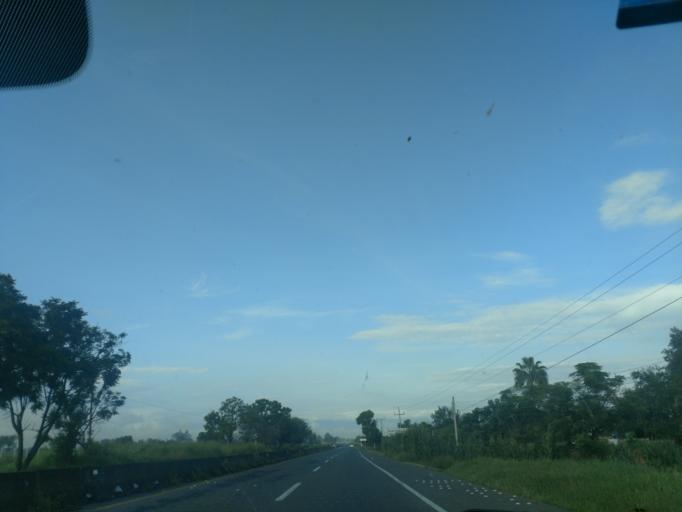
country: MX
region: Jalisco
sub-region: Ameca
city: Los Pocitos
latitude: 20.5475
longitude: -103.9056
